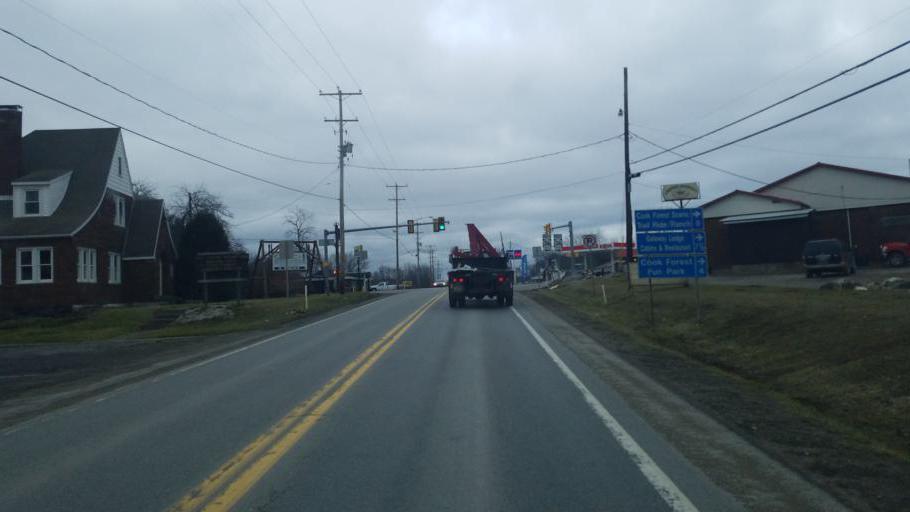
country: US
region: Pennsylvania
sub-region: Clarion County
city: Clarion
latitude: 41.3699
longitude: -79.3051
